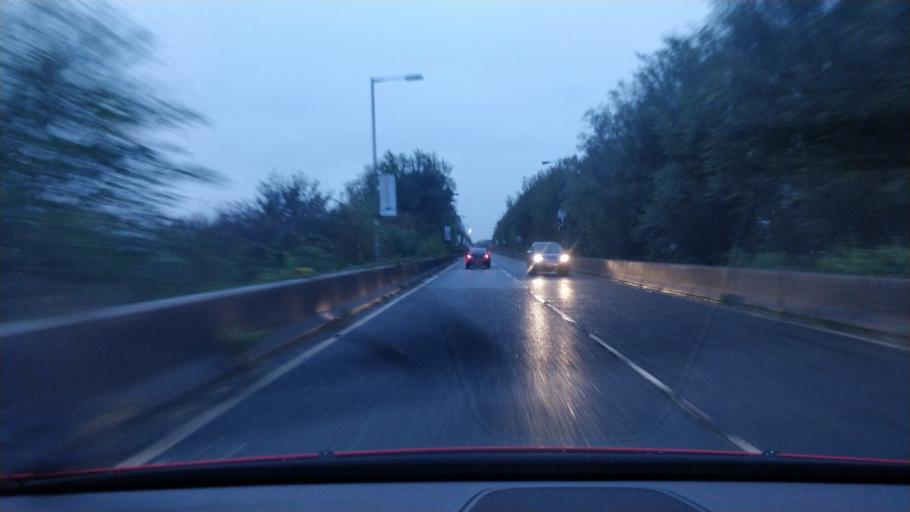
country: GB
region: England
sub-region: Lancashire
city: Great Marton
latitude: 53.7928
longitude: -3.0258
